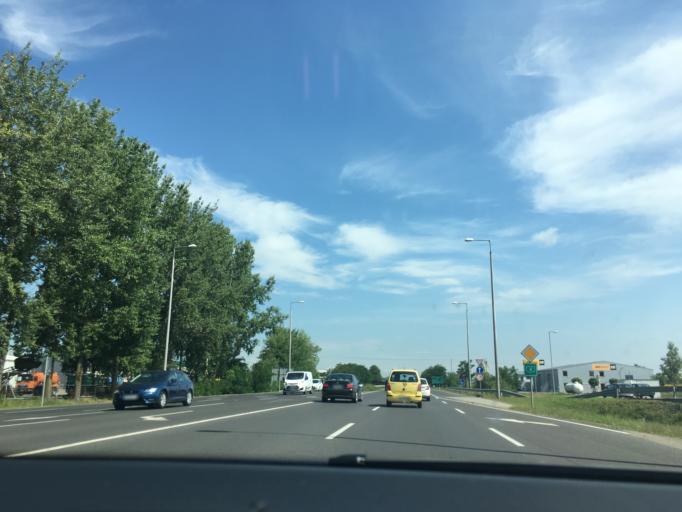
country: HU
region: Szabolcs-Szatmar-Bereg
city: Nyiregyhaza
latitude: 47.9022
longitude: 21.7120
